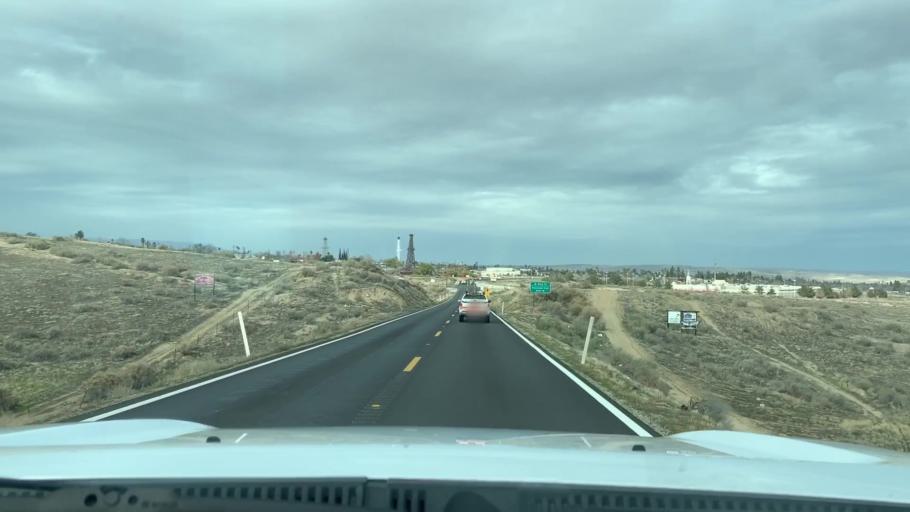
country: US
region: California
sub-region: Kern County
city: South Taft
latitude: 35.1290
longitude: -119.4430
